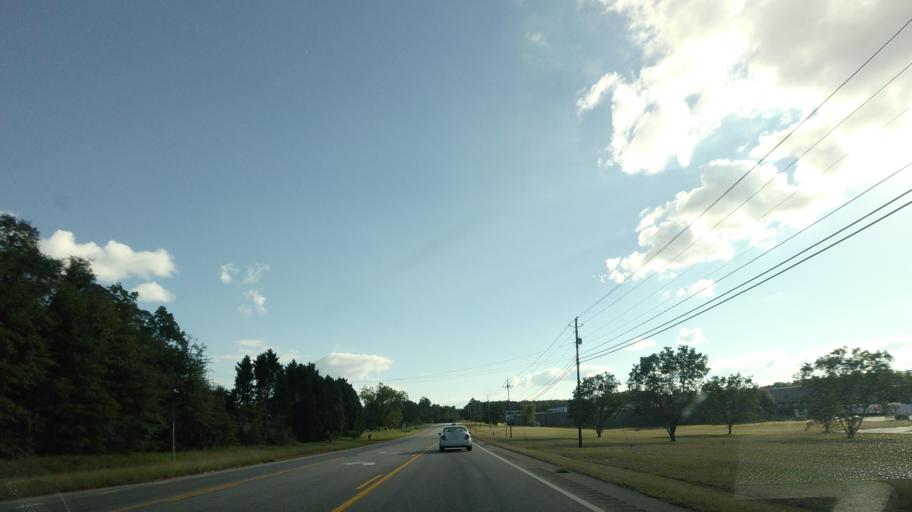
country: US
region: Georgia
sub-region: Upson County
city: Thomaston
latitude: 32.9122
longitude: -84.2938
